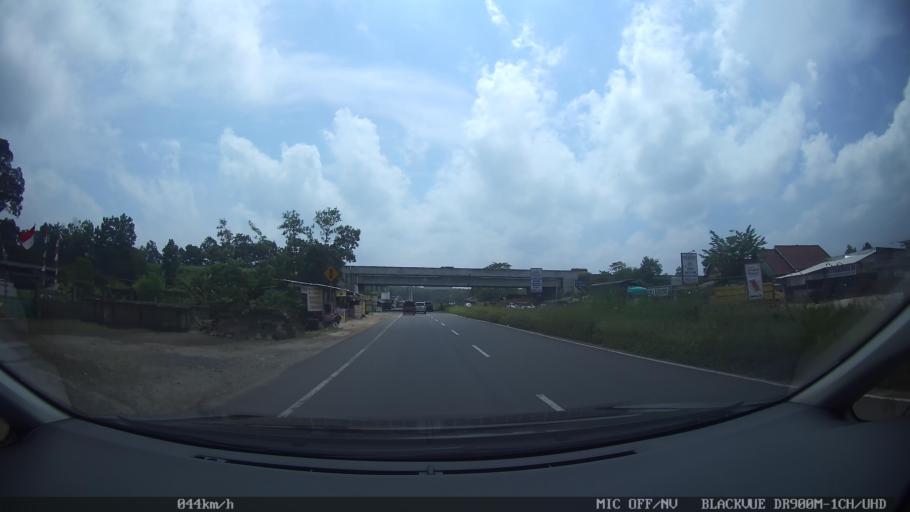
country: ID
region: Lampung
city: Kedaton
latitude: -5.3532
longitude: 105.3220
